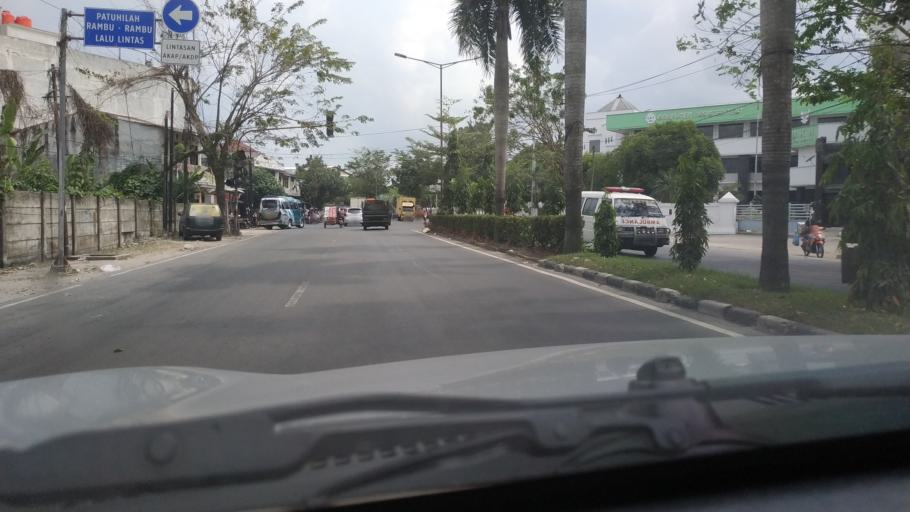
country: ID
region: North Sumatra
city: Sunggal
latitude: 3.5858
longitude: 98.6136
